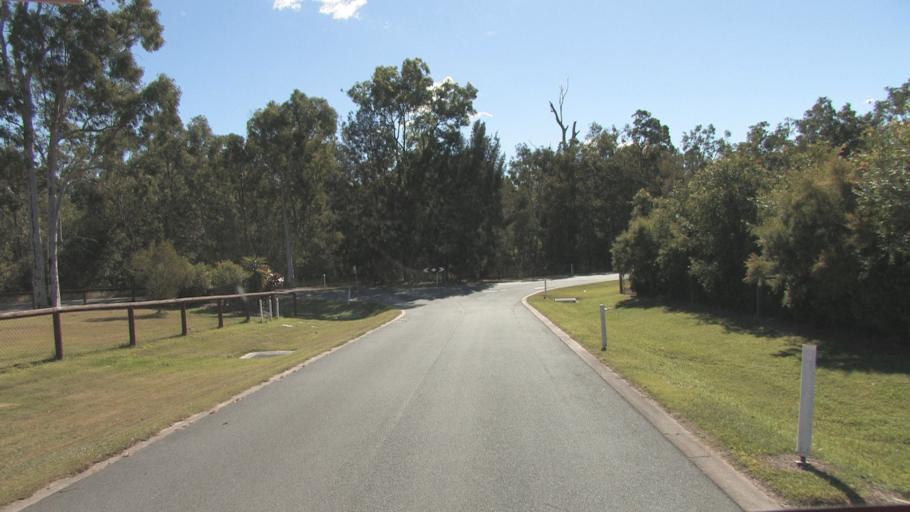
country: AU
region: Queensland
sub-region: Logan
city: North Maclean
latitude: -27.7523
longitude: 152.9588
